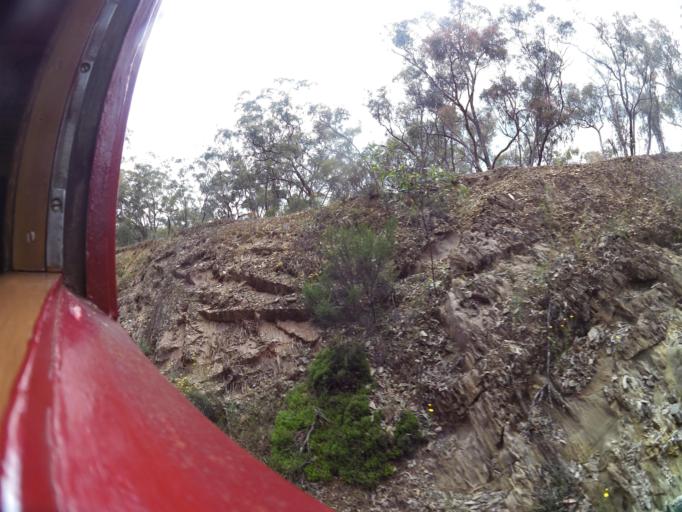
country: AU
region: Victoria
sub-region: Mount Alexander
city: Castlemaine
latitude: -37.0020
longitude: 144.1112
